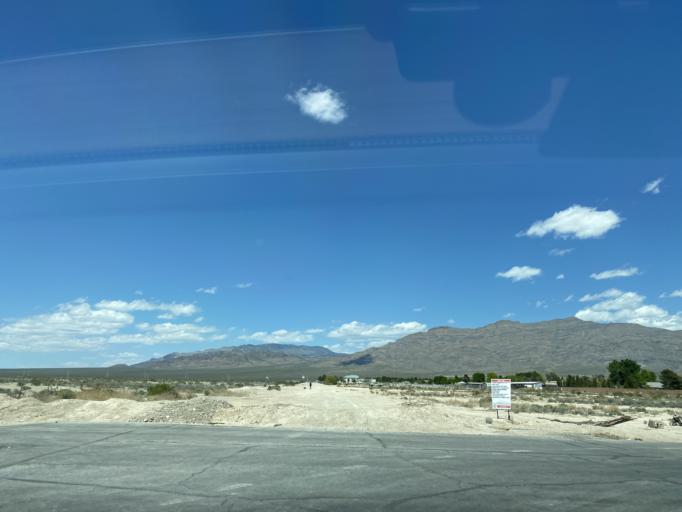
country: US
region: Nevada
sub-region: Clark County
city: North Las Vegas
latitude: 36.3107
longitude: -115.2333
